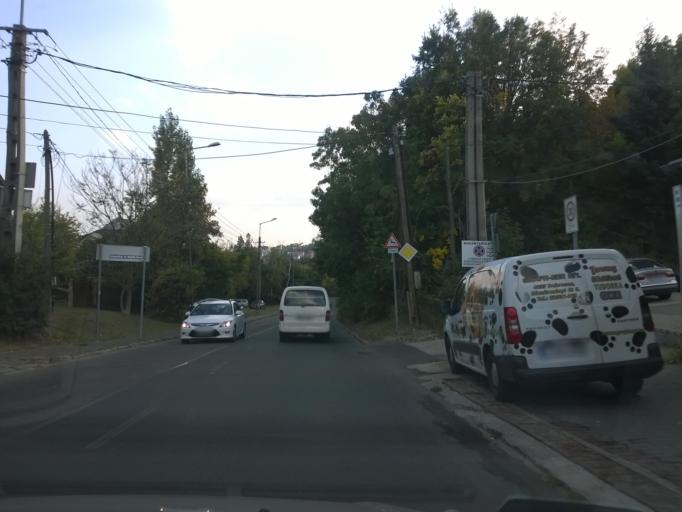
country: HU
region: Budapest
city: Budapest II. keruelet
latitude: 47.5352
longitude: 19.0153
